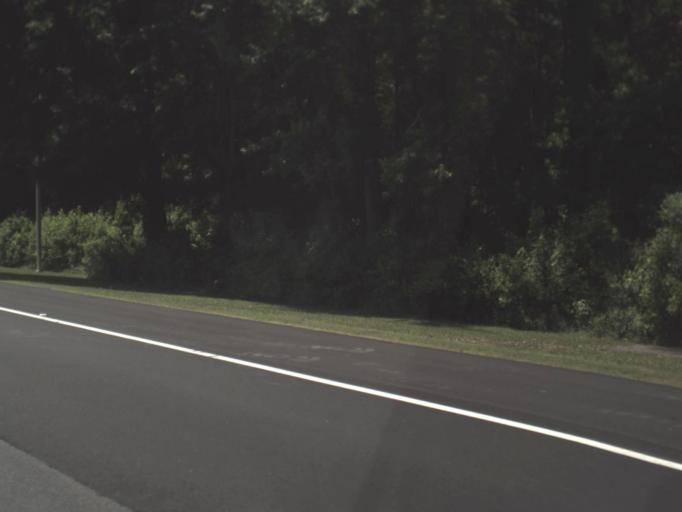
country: US
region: Florida
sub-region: Nassau County
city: Yulee
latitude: 30.6627
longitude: -81.6654
